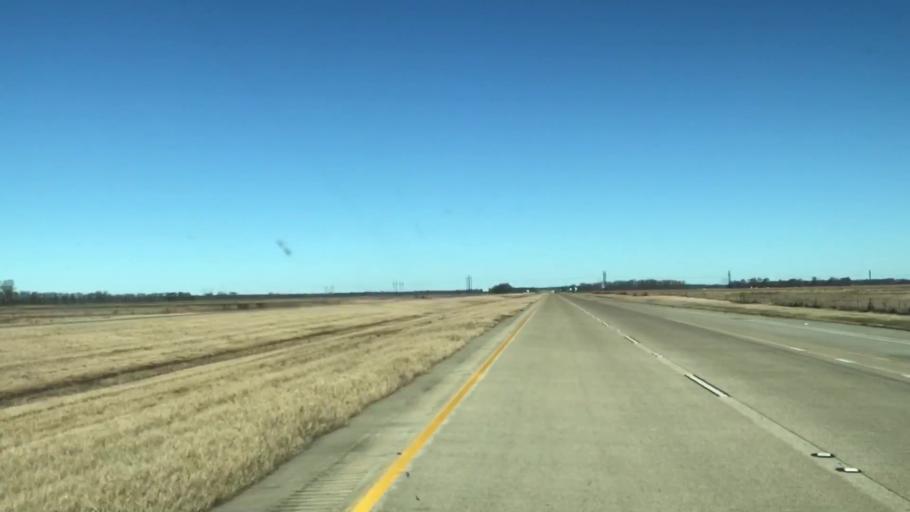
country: US
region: Louisiana
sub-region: Caddo Parish
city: Oil City
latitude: 32.7086
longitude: -93.8640
